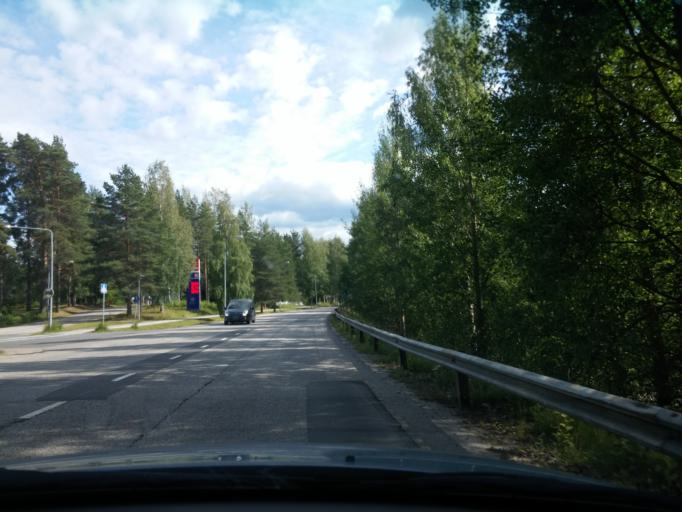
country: FI
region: Central Finland
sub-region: Keuruu
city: Keuruu
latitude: 62.2659
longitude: 24.6981
